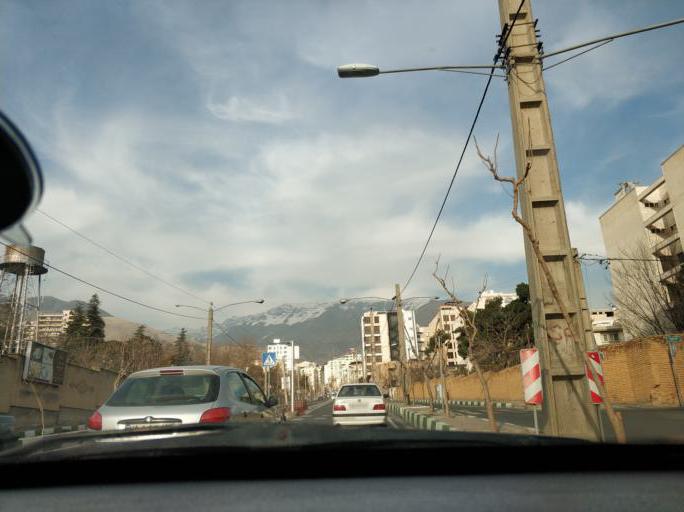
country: IR
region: Tehran
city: Tajrish
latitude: 35.8038
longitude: 51.4818
